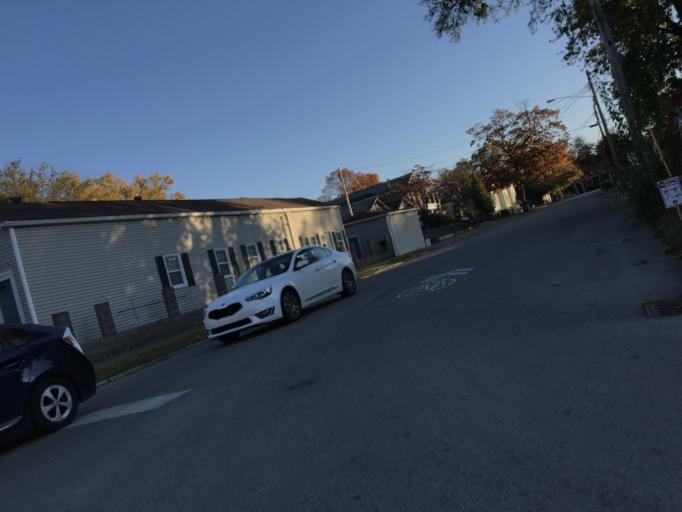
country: US
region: Kentucky
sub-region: Jefferson County
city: Louisville
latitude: 38.2453
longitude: -85.7305
